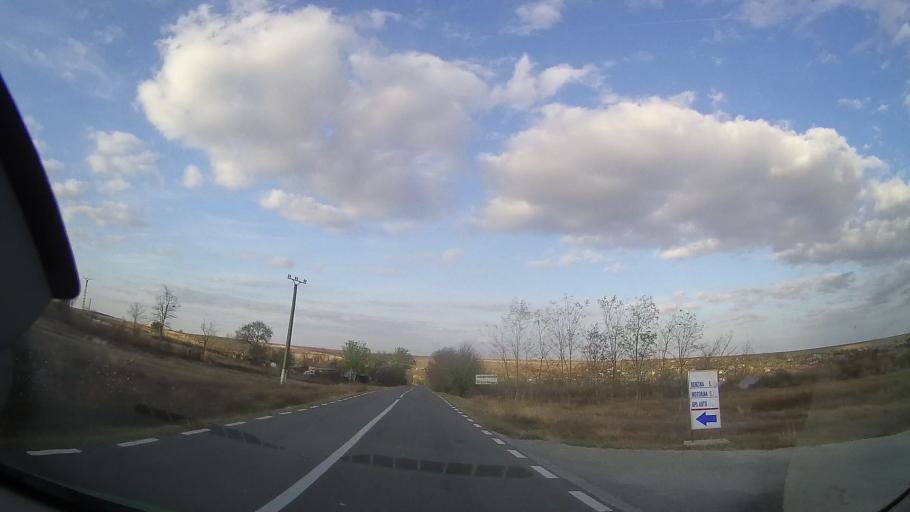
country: RO
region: Constanta
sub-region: Comuna Independenta
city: Independenta
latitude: 43.9497
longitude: 28.0748
